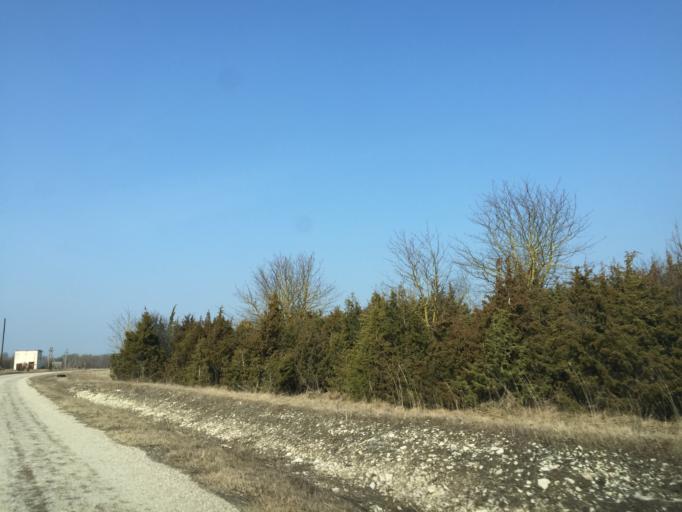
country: EE
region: Saare
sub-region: Orissaare vald
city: Orissaare
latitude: 58.4831
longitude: 23.1204
